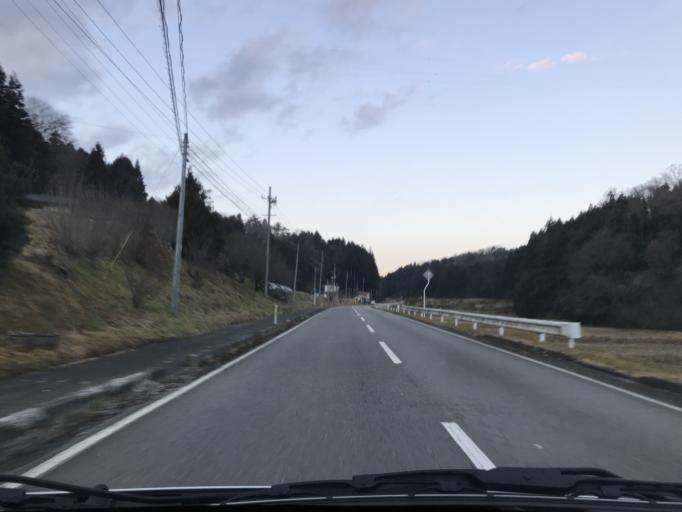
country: JP
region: Iwate
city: Ichinoseki
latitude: 38.8140
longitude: 141.1156
